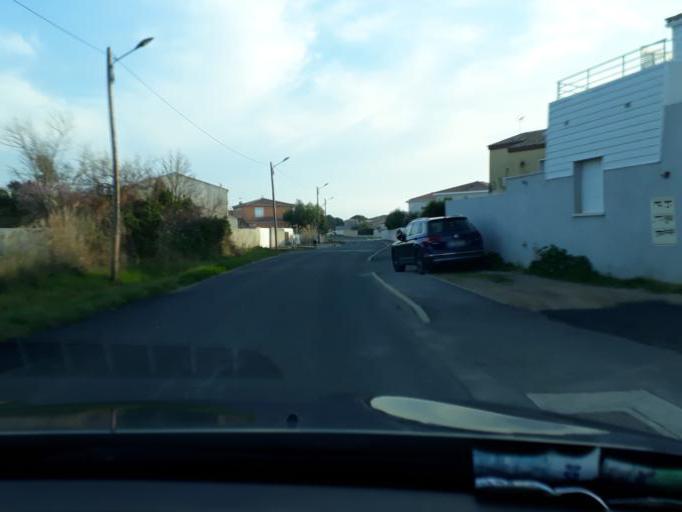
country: FR
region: Languedoc-Roussillon
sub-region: Departement de l'Herault
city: Marseillan
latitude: 43.3411
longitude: 3.5332
